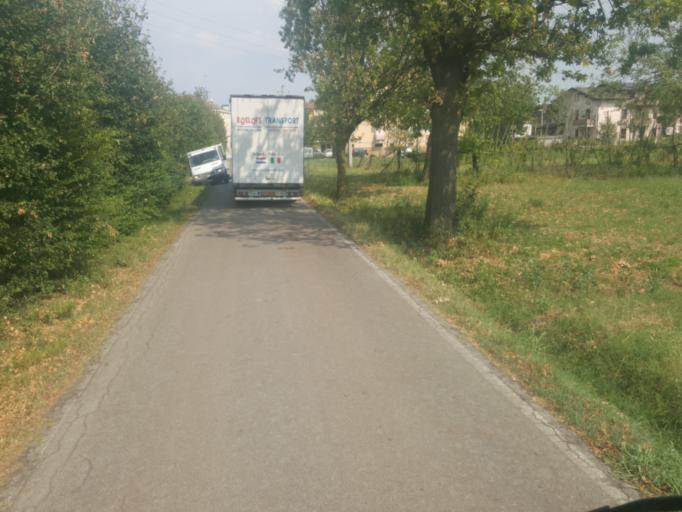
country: IT
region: Emilia-Romagna
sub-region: Provincia di Modena
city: Gaggio
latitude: 44.6363
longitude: 11.0095
